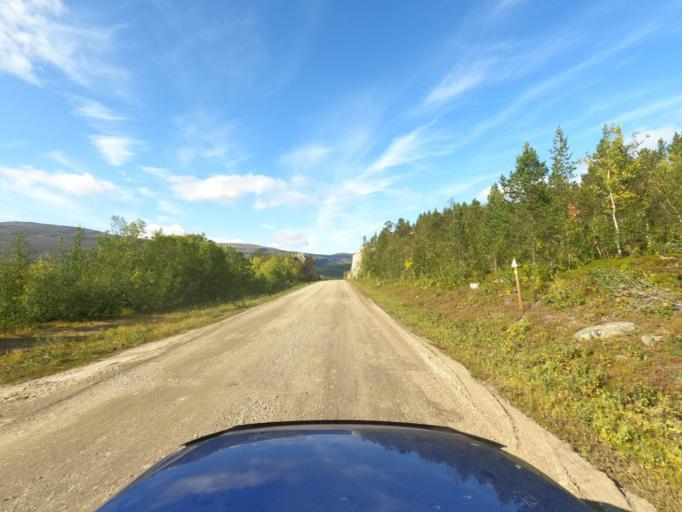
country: NO
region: Finnmark Fylke
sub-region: Porsanger
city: Lakselv
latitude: 69.8897
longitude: 25.0047
